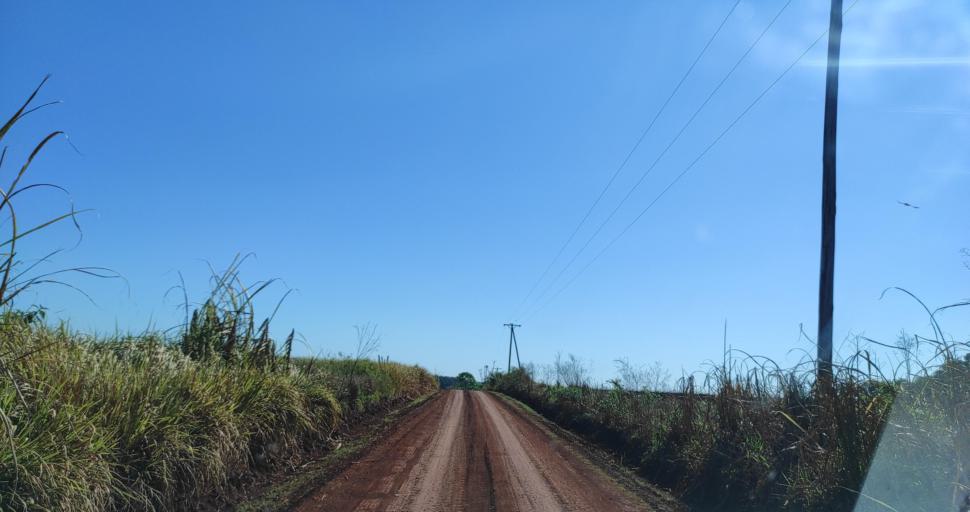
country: AR
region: Misiones
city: Capiovi
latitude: -26.9165
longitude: -55.0217
